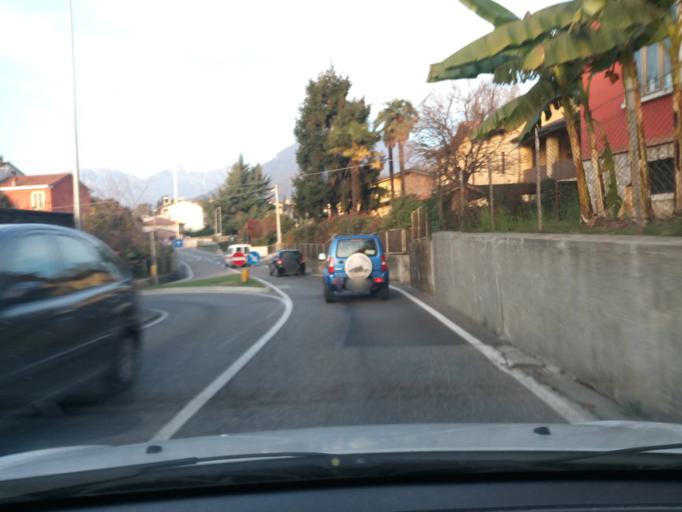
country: IT
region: Veneto
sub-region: Provincia di Vicenza
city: Schio
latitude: 45.7165
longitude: 11.3514
